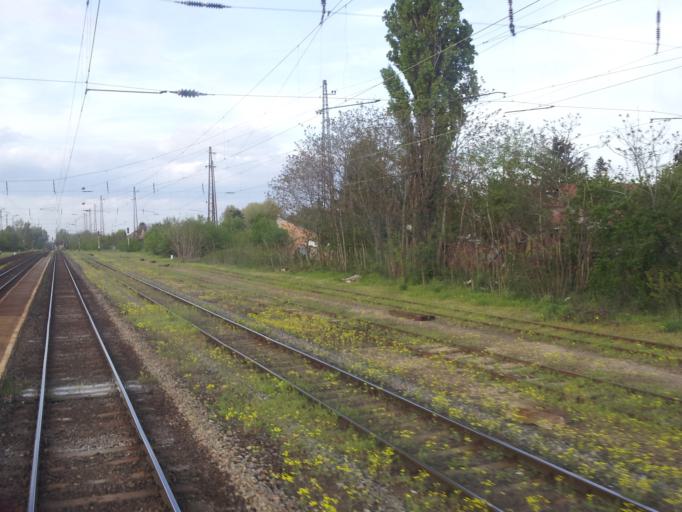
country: HU
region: Budapest
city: Budapest XV. keruelet
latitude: 47.5680
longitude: 19.1135
